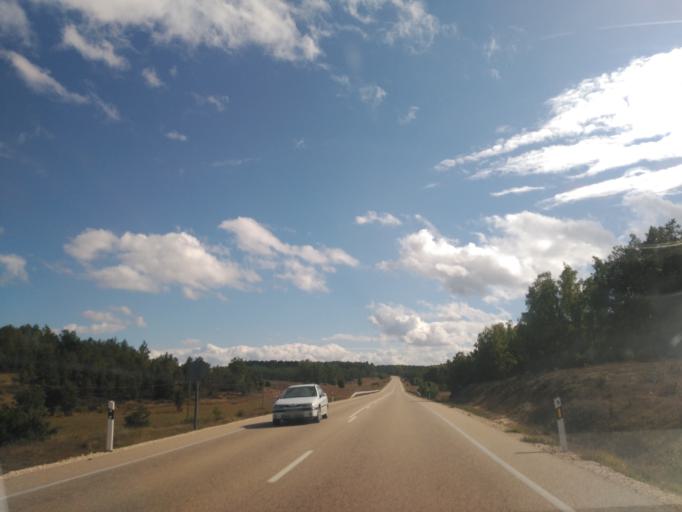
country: ES
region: Castille and Leon
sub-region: Provincia de Burgos
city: Hacinas
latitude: 41.9544
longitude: -3.2914
